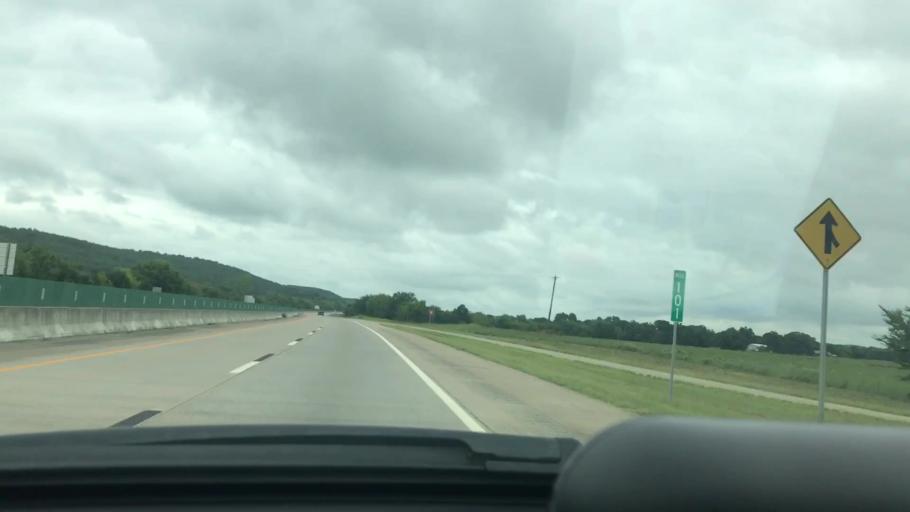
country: US
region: Oklahoma
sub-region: Pittsburg County
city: Krebs
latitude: 35.0603
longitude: -95.7062
